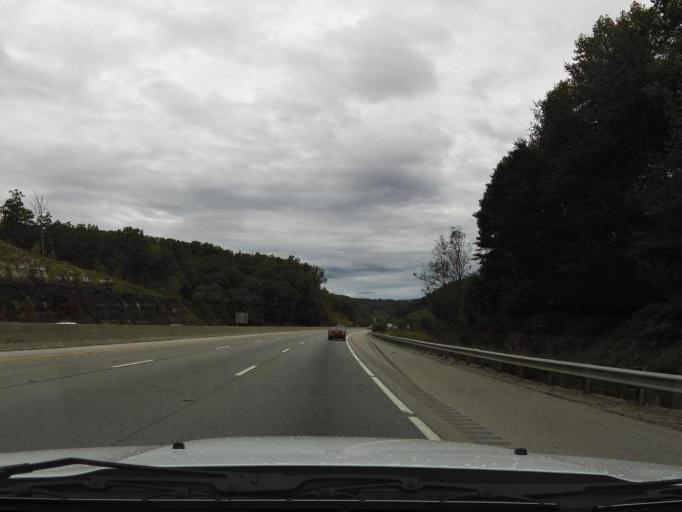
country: US
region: Kentucky
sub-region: Rockcastle County
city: Mount Vernon
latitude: 37.2313
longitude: -84.2243
